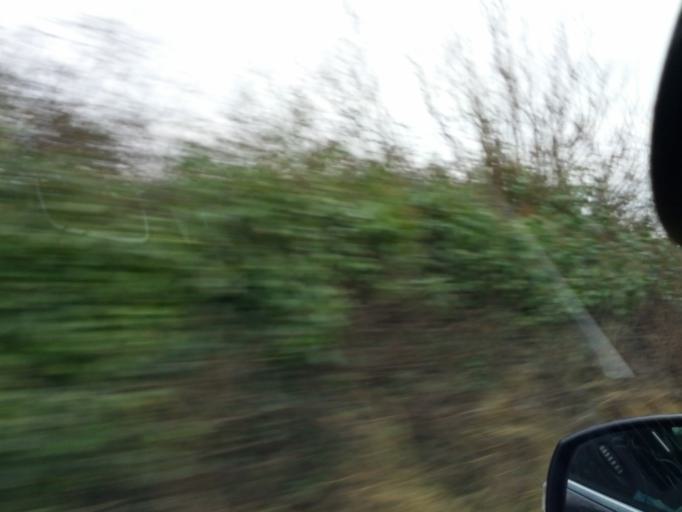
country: IE
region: Connaught
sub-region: County Galway
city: Athenry
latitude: 53.2315
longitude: -8.7636
